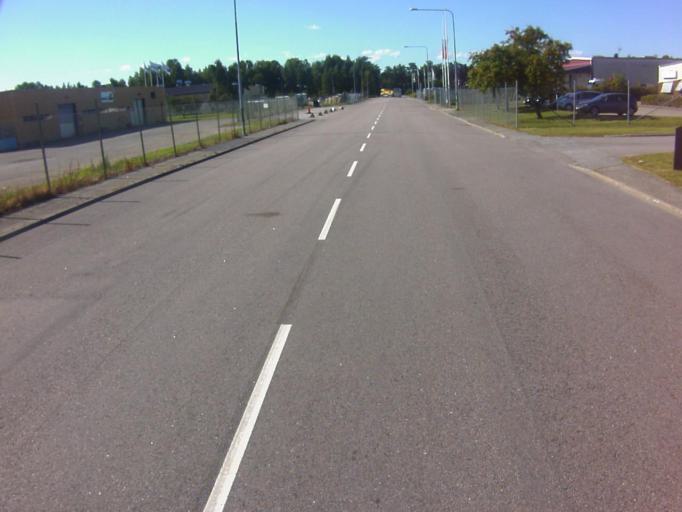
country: SE
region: Soedermanland
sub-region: Eskilstuna Kommun
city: Eskilstuna
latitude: 59.3878
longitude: 16.4891
